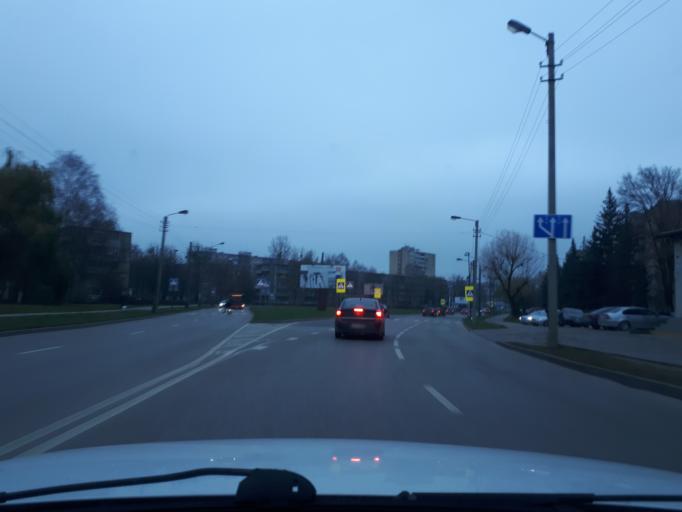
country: LT
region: Kauno apskritis
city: Dainava (Kaunas)
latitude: 54.9160
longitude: 23.9550
